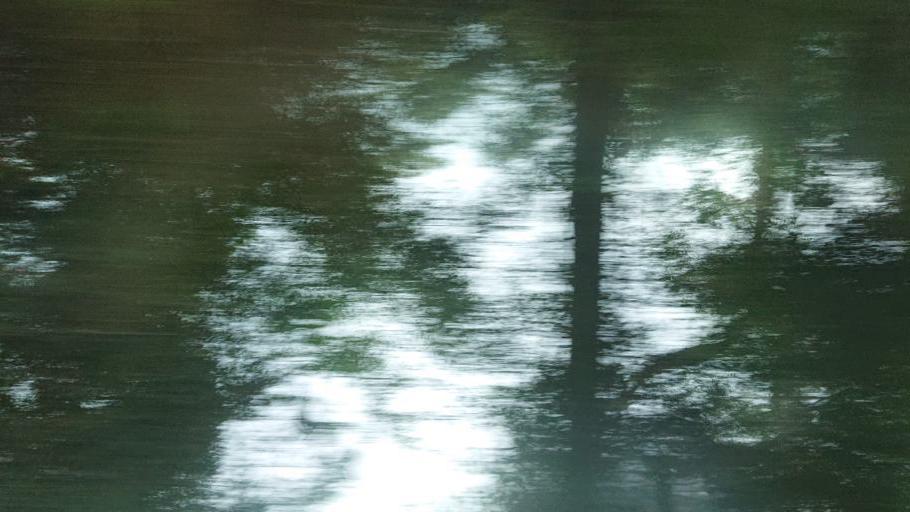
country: TW
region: Taiwan
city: Lugu
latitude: 23.5908
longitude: 120.7127
